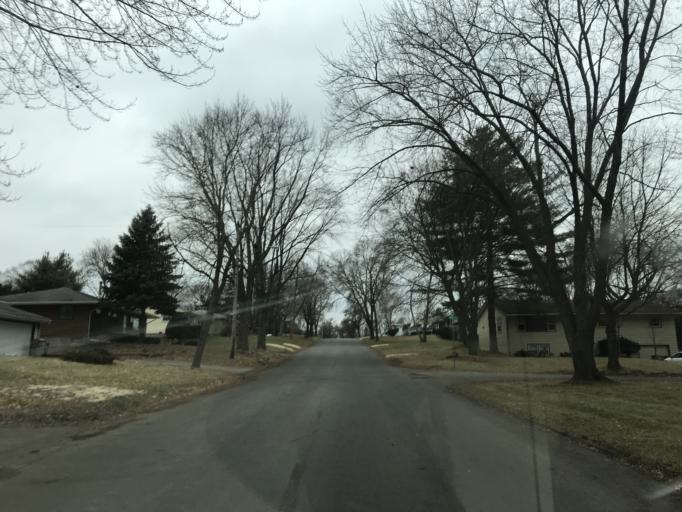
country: US
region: Wisconsin
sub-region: Dane County
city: Monona
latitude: 43.0686
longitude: -89.3132
